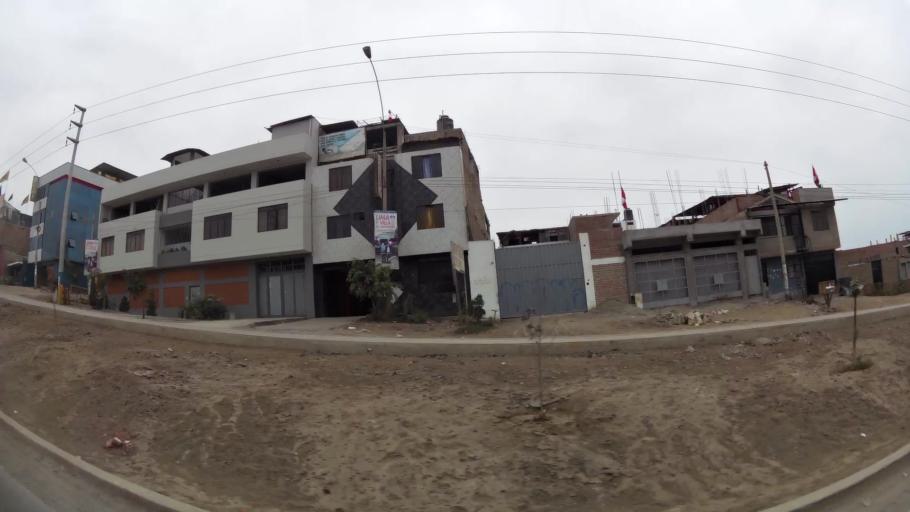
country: PE
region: Lima
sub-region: Lima
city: Surco
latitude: -12.2087
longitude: -76.9579
